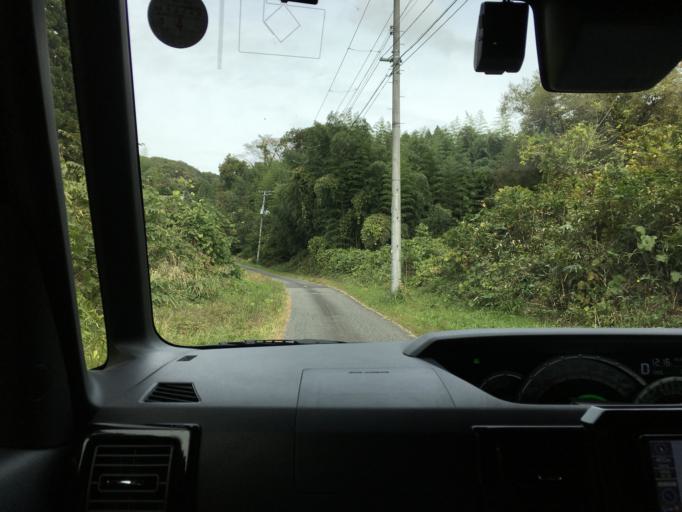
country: JP
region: Iwate
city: Mizusawa
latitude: 39.0273
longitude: 141.3569
